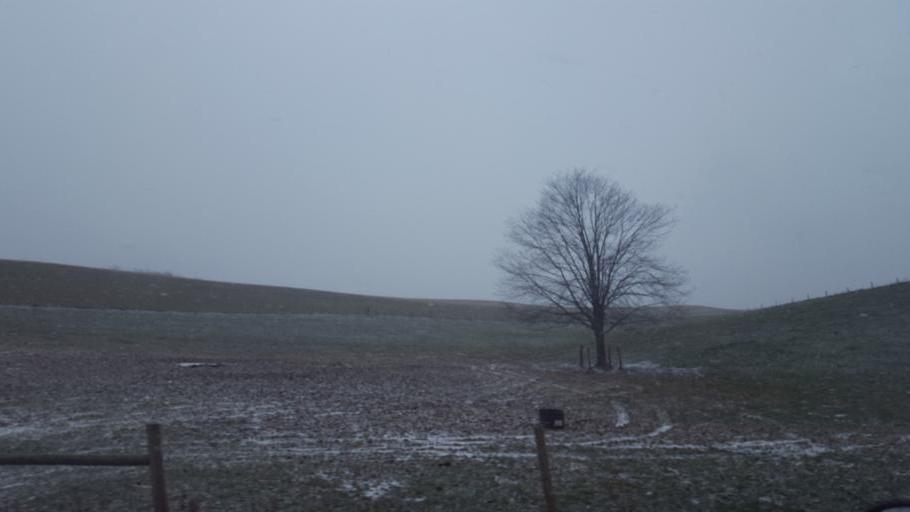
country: US
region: Ohio
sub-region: Tuscarawas County
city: Sugarcreek
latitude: 40.4782
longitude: -81.7328
